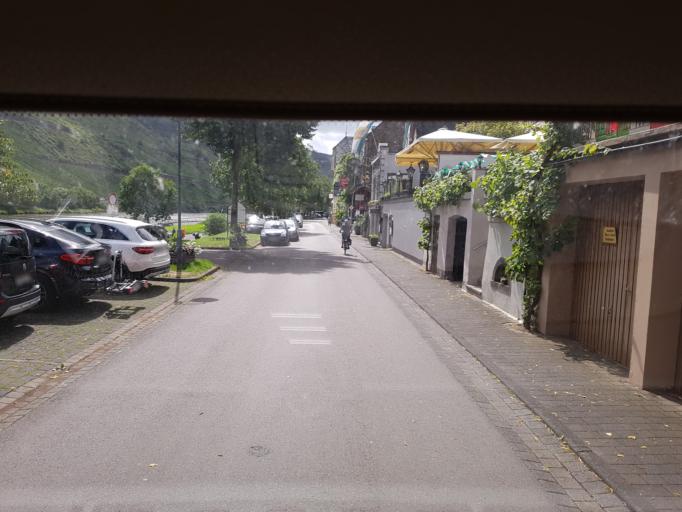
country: DE
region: Rheinland-Pfalz
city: Reil
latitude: 50.0212
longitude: 7.1179
